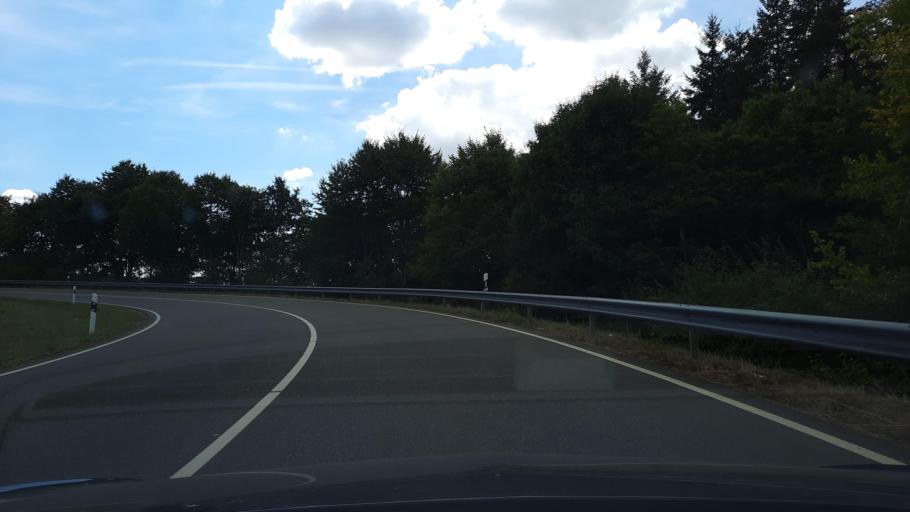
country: DE
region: Rheinland-Pfalz
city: Prum
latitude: 50.1982
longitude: 6.4309
